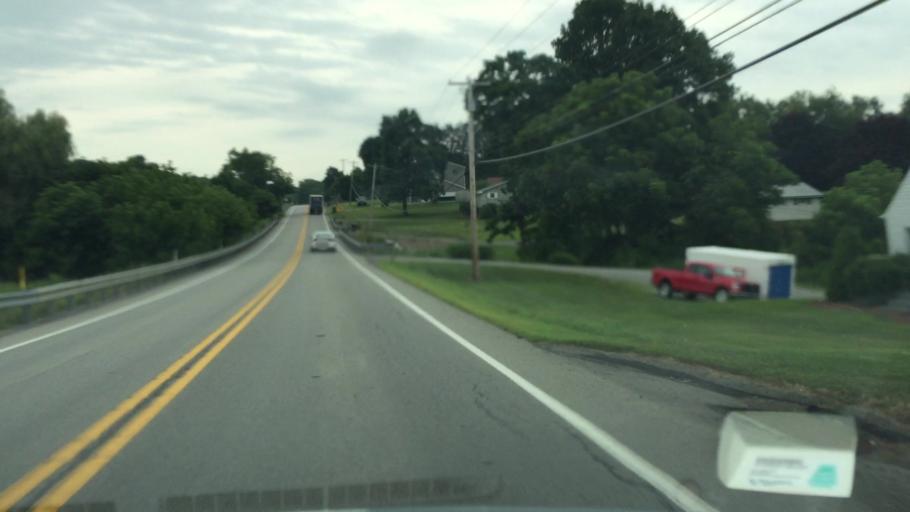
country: US
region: Pennsylvania
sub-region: Butler County
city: Nixon
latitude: 40.7239
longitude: -79.9074
